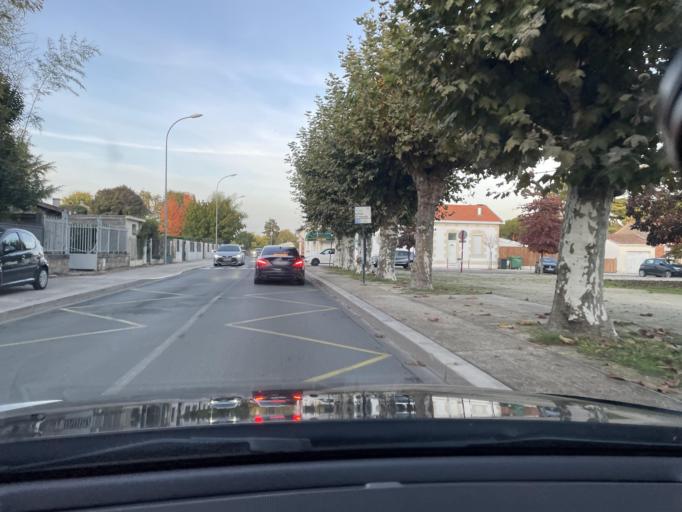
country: FR
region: Aquitaine
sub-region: Departement de la Gironde
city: Villenave-d'Ornon
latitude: 44.7716
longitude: -0.5407
